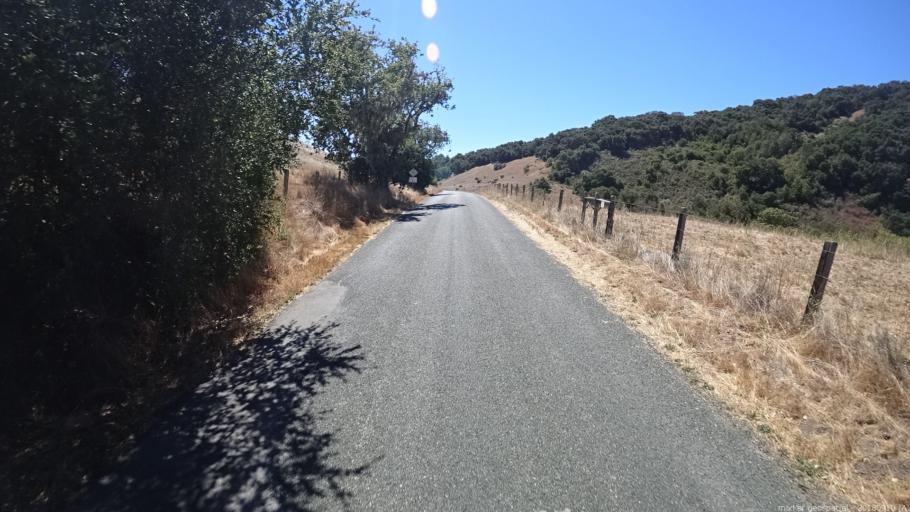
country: US
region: California
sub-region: Monterey County
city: Carmel Valley Village
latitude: 36.4723
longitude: -121.8021
